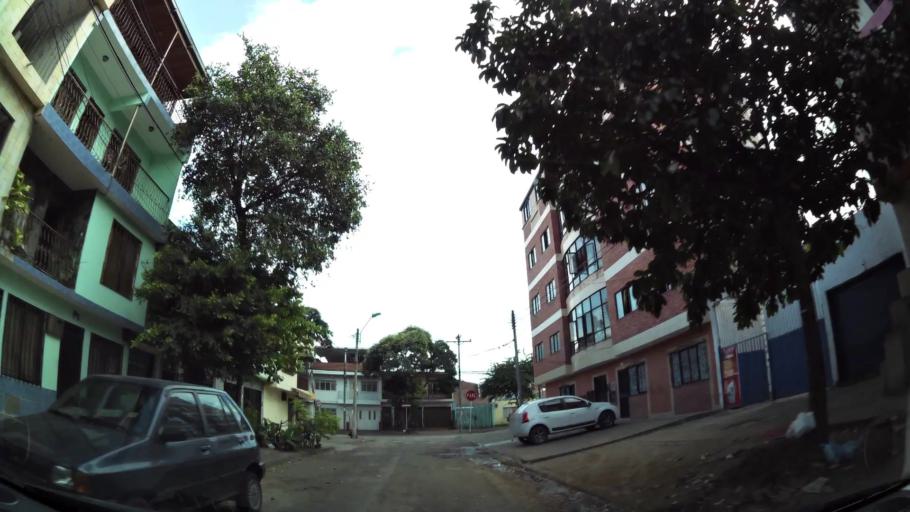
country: CO
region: Valle del Cauca
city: Cali
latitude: 3.4624
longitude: -76.5097
